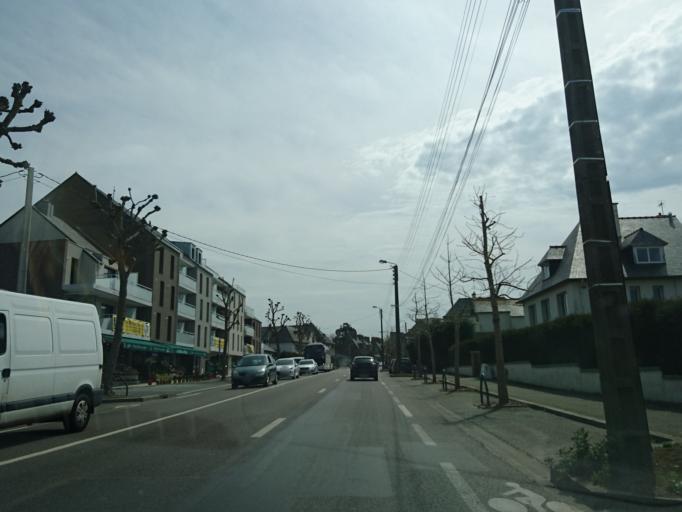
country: FR
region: Brittany
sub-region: Departement d'Ille-et-Vilaine
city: Saint-Malo
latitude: 48.6342
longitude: -2.0079
